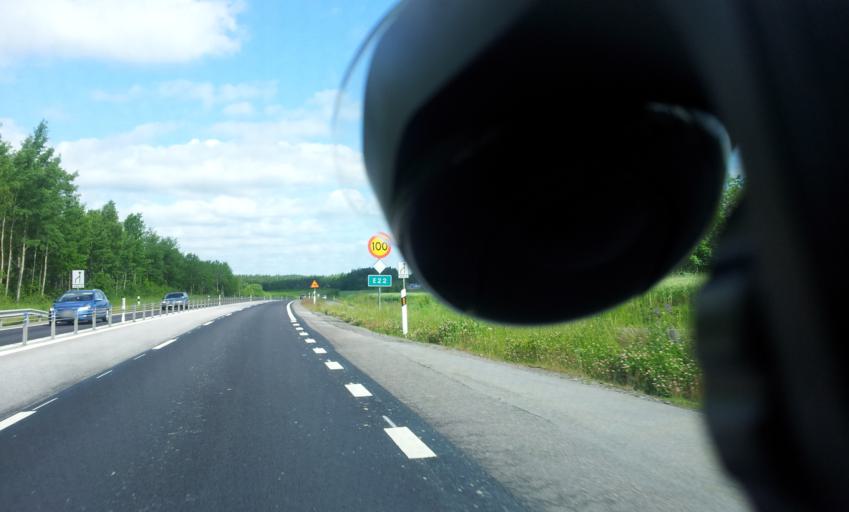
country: SE
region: OEstergoetland
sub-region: Soderkopings Kommun
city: Soederkoeping
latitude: 58.5096
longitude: 16.2918
